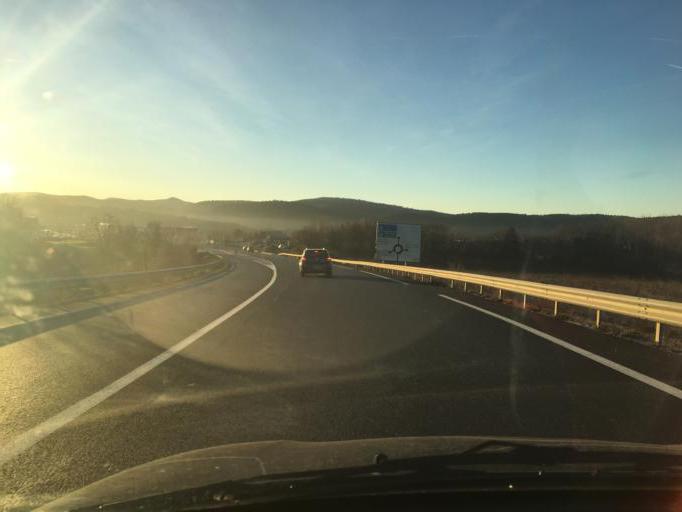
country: FR
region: Provence-Alpes-Cote d'Azur
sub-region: Departement du Var
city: Les Arcs
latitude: 43.4558
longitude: 6.4891
